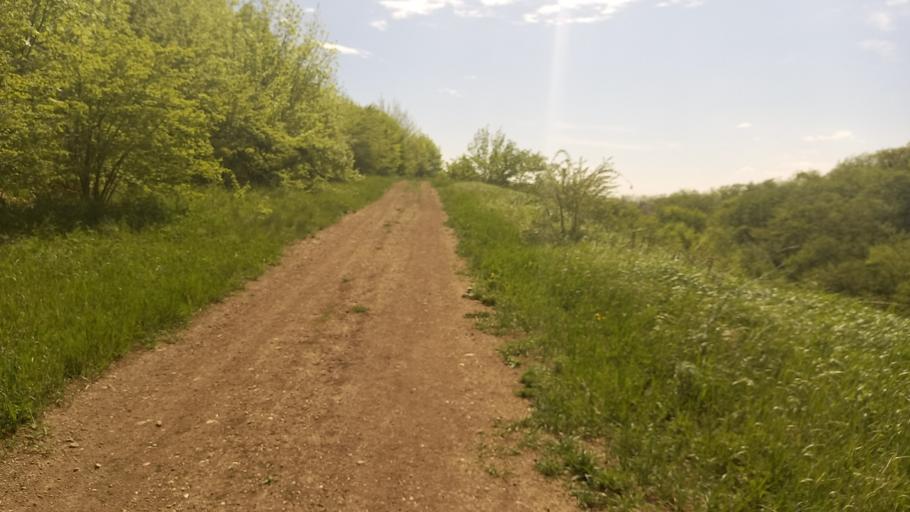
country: RU
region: Stavropol'skiy
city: Zheleznovodsk
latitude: 44.0904
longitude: 43.0310
